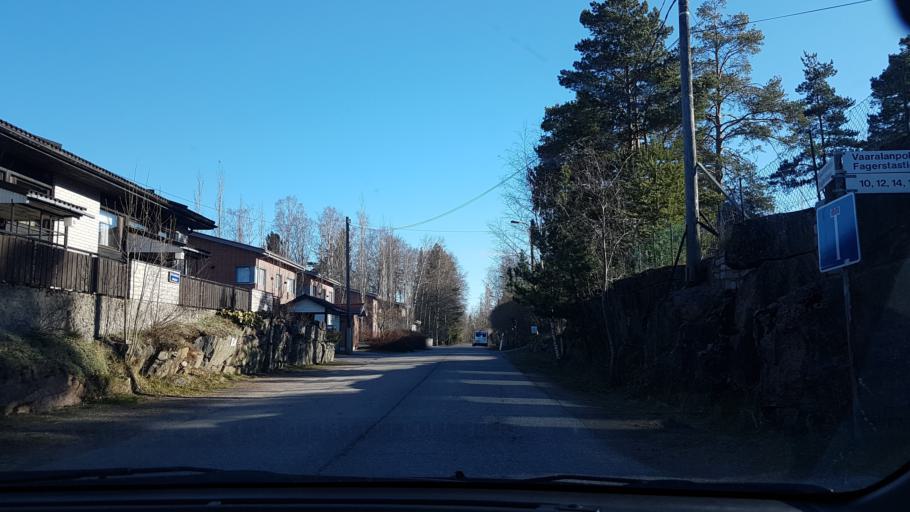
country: FI
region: Uusimaa
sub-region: Helsinki
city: Vantaa
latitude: 60.2685
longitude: 25.0919
